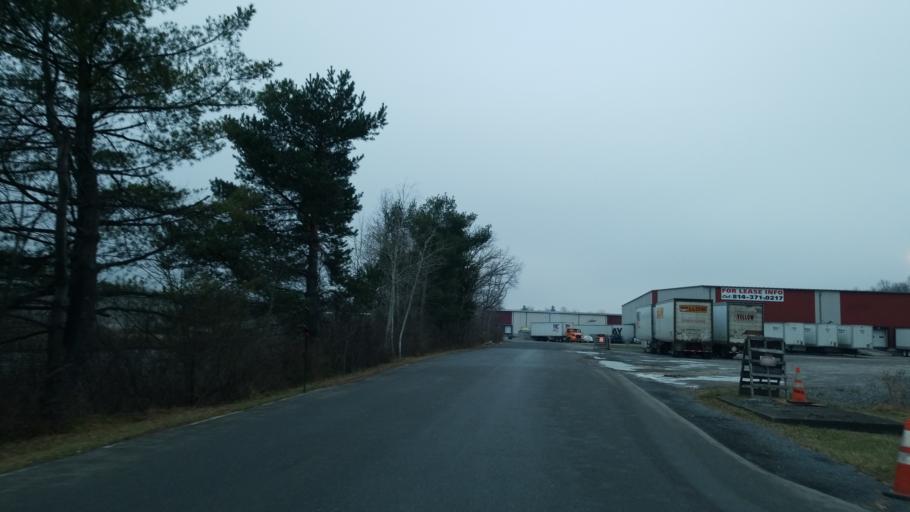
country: US
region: Pennsylvania
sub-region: Clearfield County
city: DuBois
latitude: 41.1166
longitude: -78.7316
